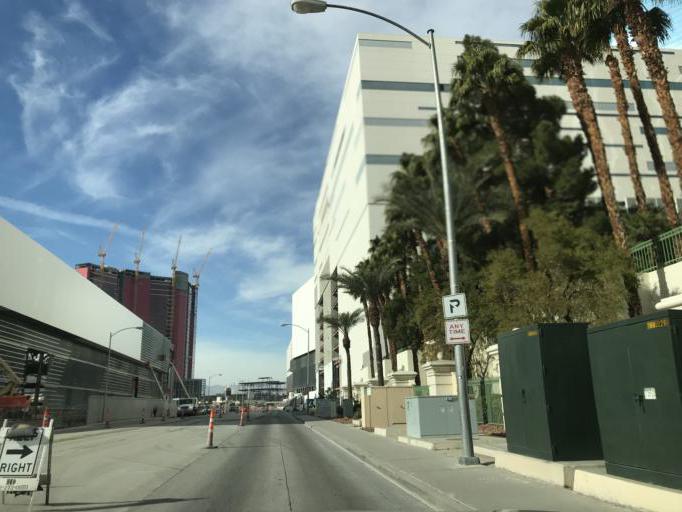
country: US
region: Nevada
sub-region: Clark County
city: Winchester
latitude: 36.1363
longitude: -115.1565
